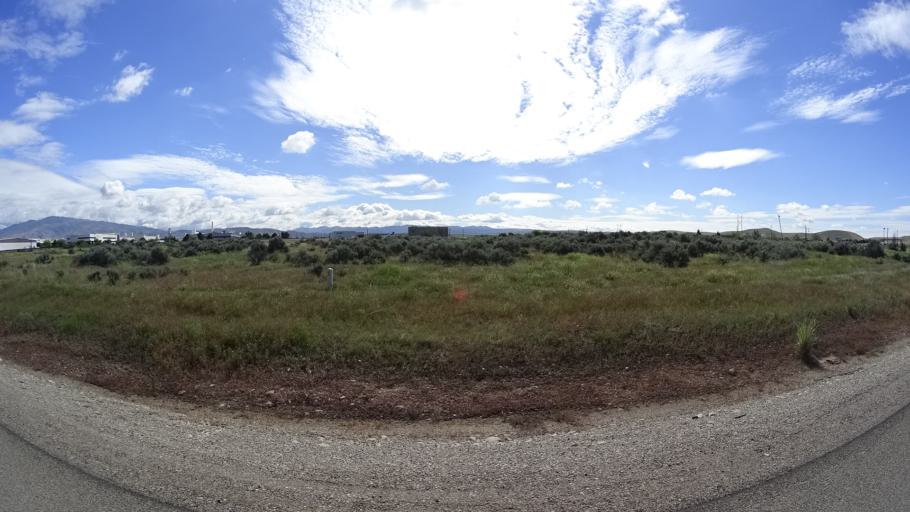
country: US
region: Idaho
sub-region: Ada County
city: Boise
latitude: 43.5192
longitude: -116.1514
